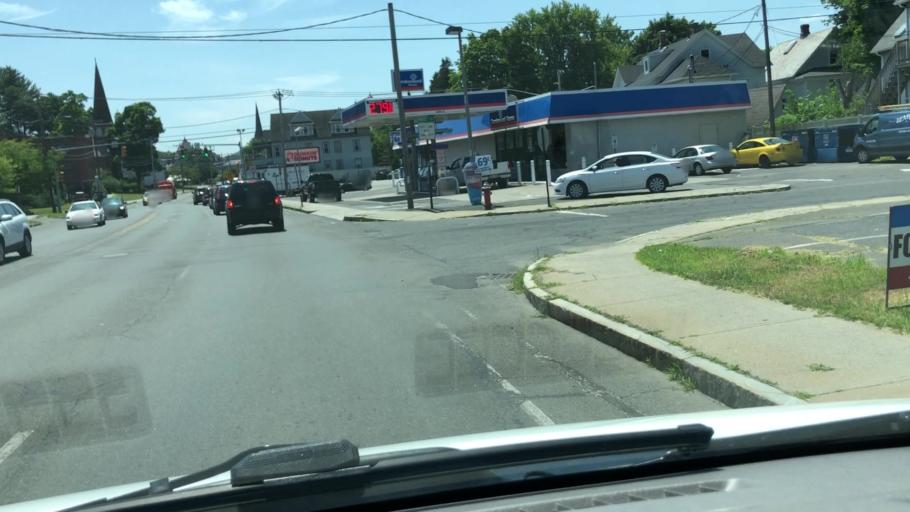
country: US
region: Massachusetts
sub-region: Hampshire County
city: Northampton
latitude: 42.3248
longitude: -72.6331
